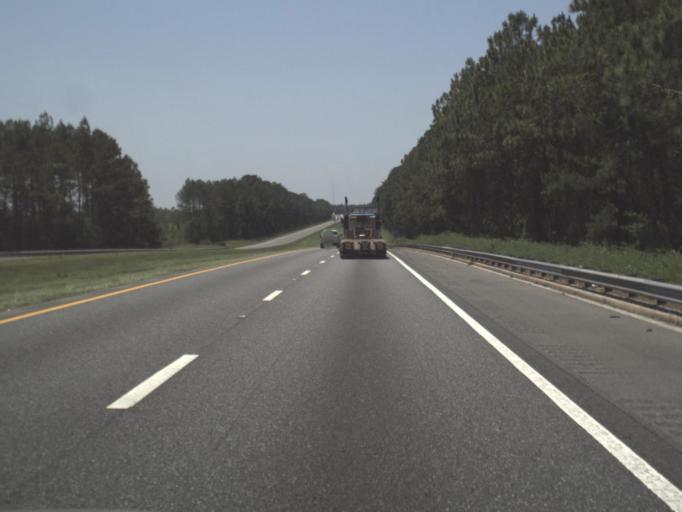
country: US
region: Florida
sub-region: Baker County
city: Macclenny
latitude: 30.2815
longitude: -82.0502
